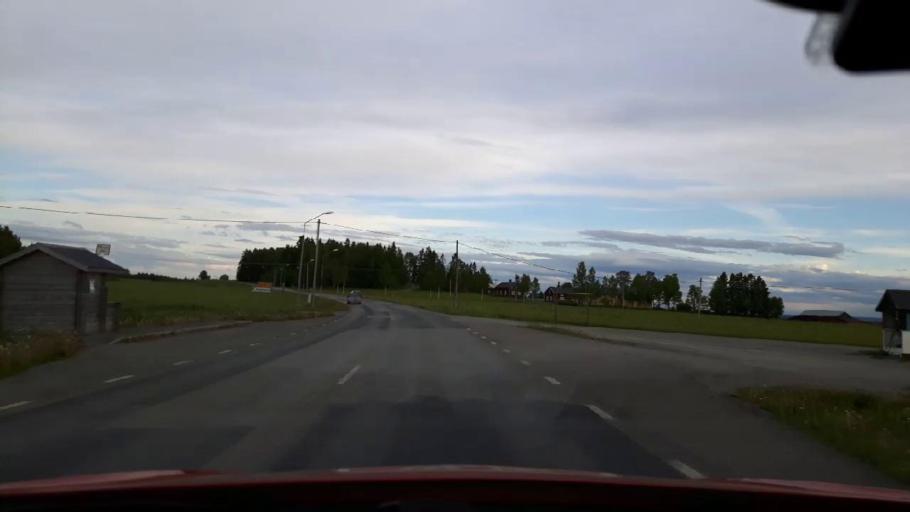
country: SE
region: Jaemtland
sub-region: OEstersunds Kommun
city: Ostersund
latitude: 63.1004
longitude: 14.4346
